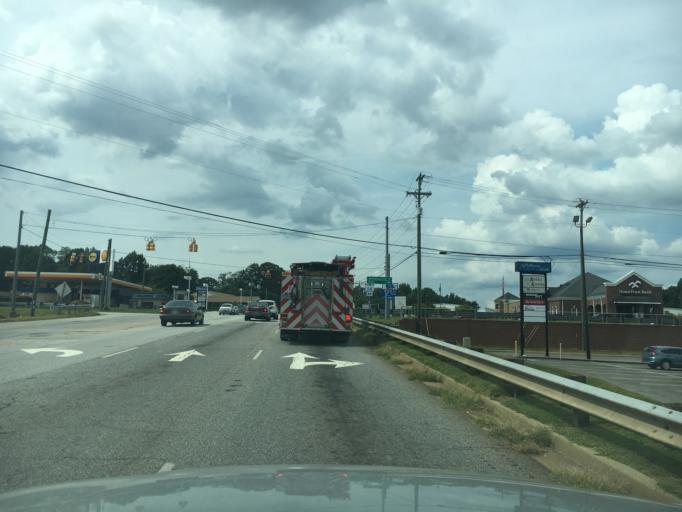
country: US
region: South Carolina
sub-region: Greenville County
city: Five Forks
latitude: 34.8509
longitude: -82.2298
